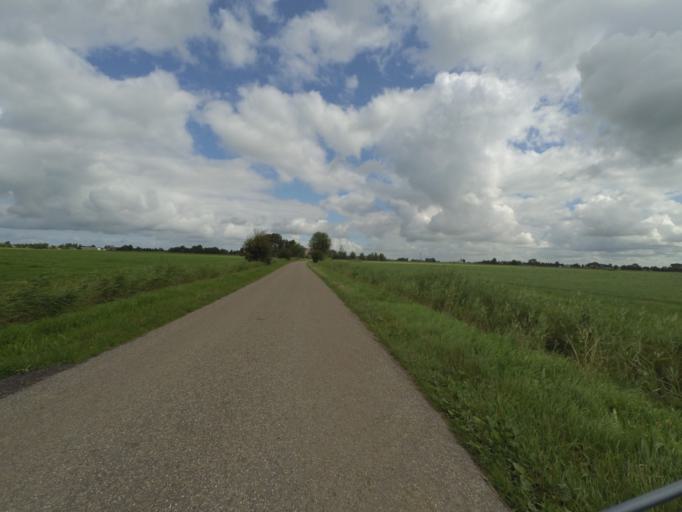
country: NL
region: Friesland
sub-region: Gemeente Kollumerland en Nieuwkruisland
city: Kollum
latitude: 53.2667
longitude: 6.1750
